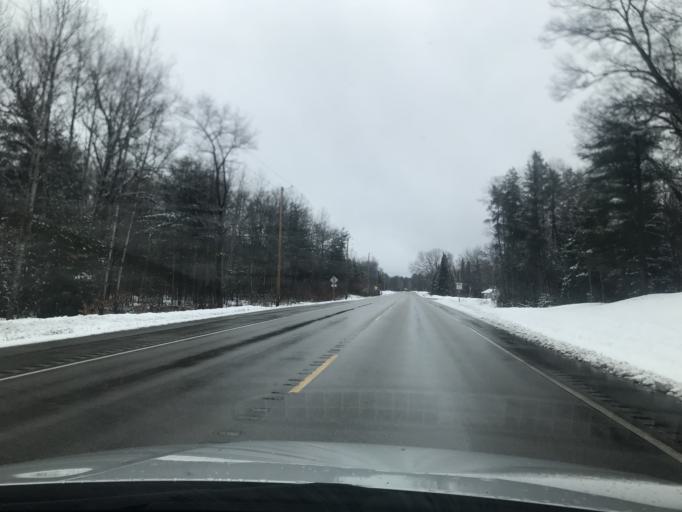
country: US
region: Wisconsin
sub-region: Marinette County
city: Peshtigo
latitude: 45.1655
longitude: -87.7279
